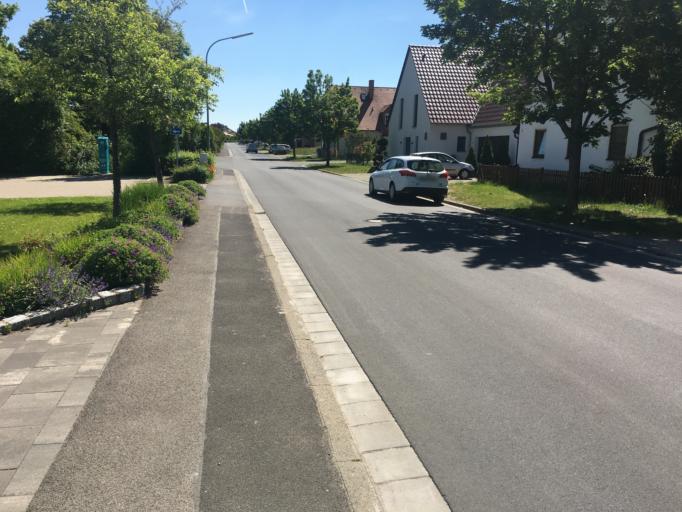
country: DE
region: Bavaria
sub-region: Regierungsbezirk Unterfranken
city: Rothlein
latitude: 49.9814
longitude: 10.2120
